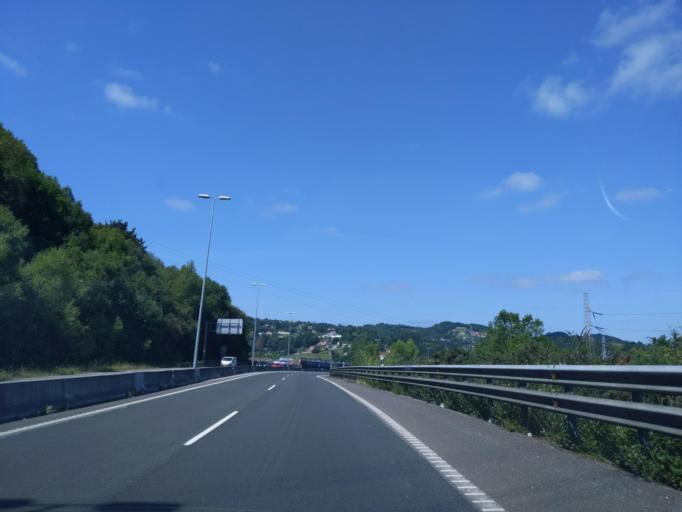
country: ES
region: Asturias
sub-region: Province of Asturias
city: Sama
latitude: 43.3029
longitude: -5.6955
